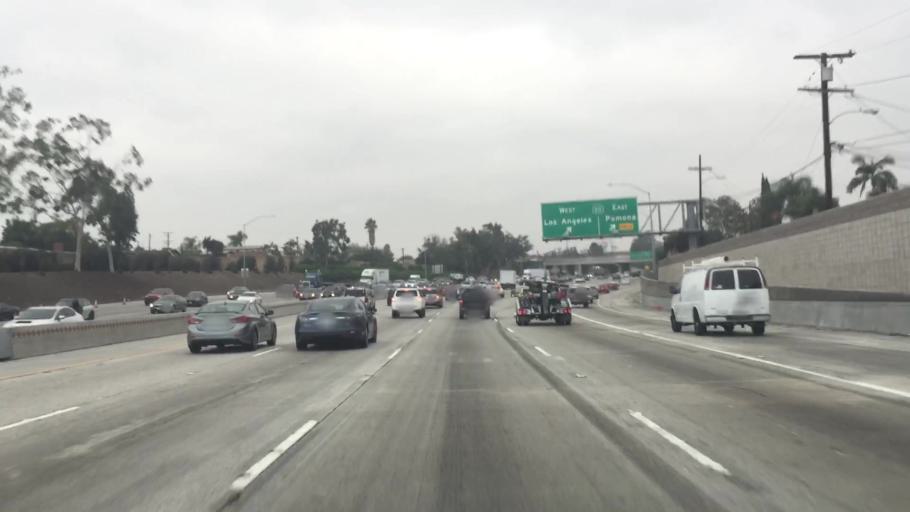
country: US
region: California
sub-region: Los Angeles County
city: East Los Angeles
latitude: 34.0264
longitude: -118.1722
